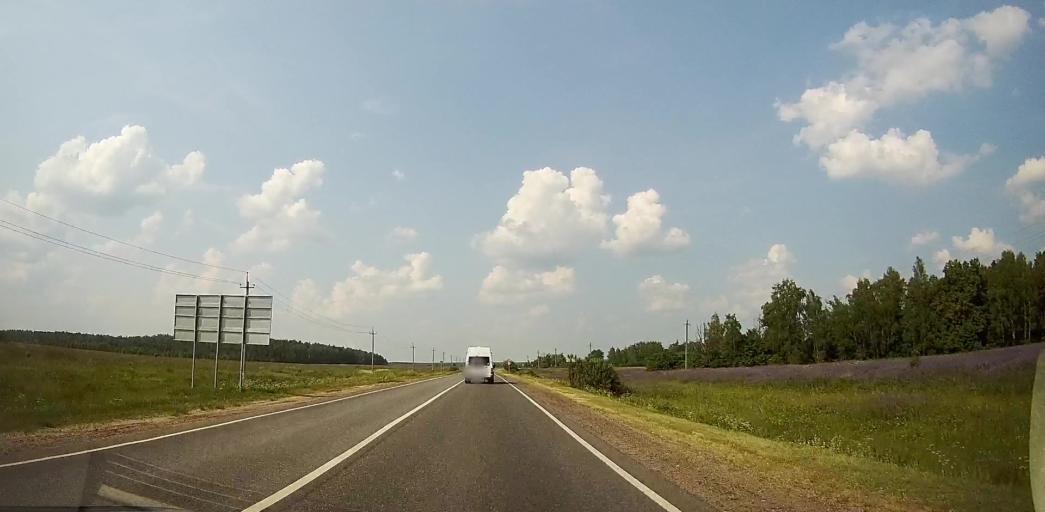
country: RU
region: Moskovskaya
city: Stupino
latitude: 54.9589
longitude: 38.1237
